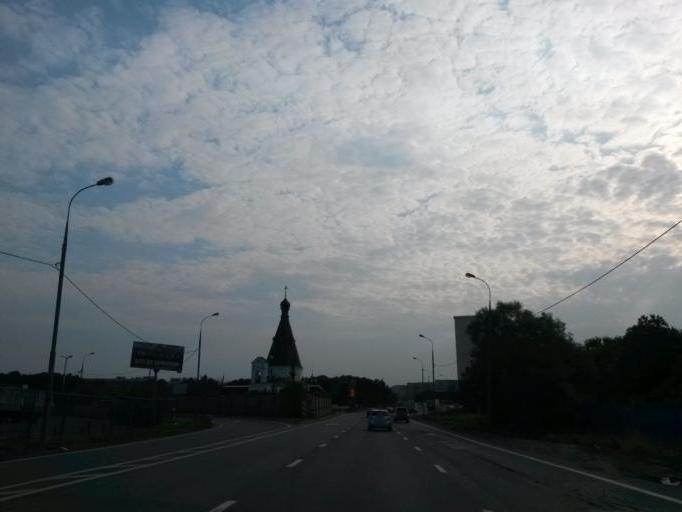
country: RU
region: Moscow
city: Annino
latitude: 55.5738
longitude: 37.6033
